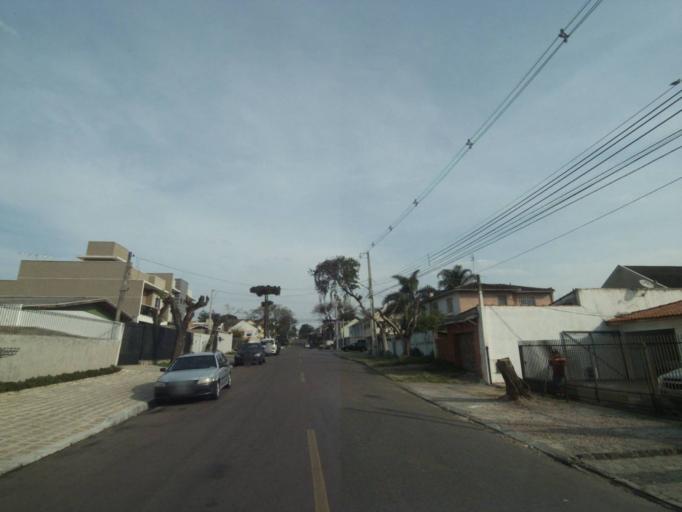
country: BR
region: Parana
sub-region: Curitiba
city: Curitiba
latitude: -25.4592
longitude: -49.3158
